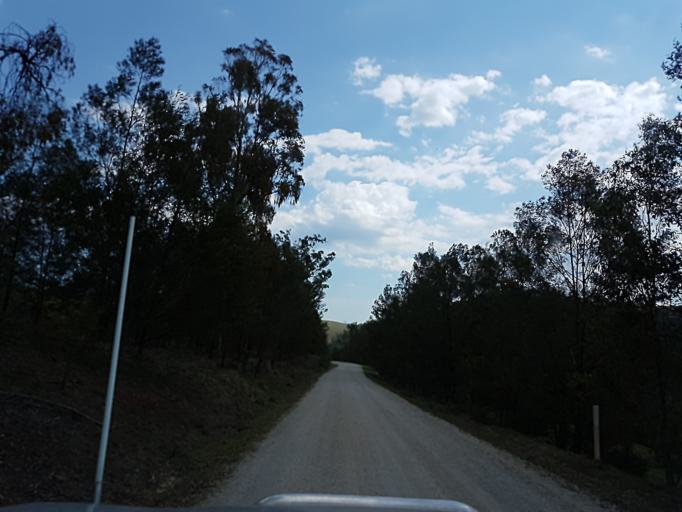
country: AU
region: Victoria
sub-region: East Gippsland
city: Lakes Entrance
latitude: -37.4812
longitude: 148.2390
